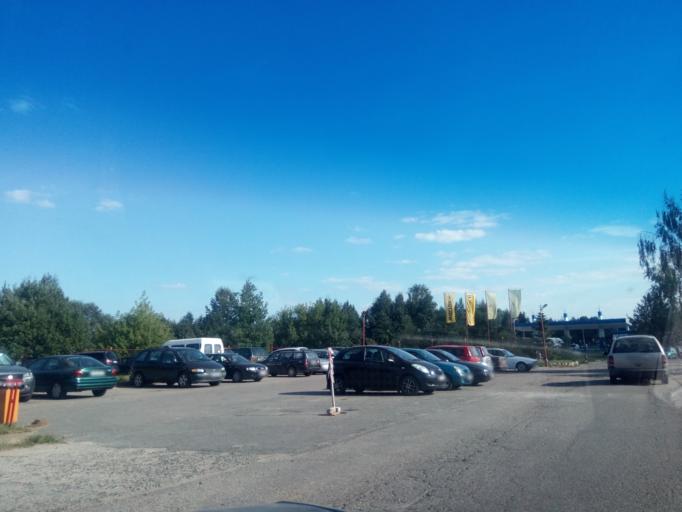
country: BY
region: Vitebsk
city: Navapolatsk
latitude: 55.5446
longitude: 28.6656
